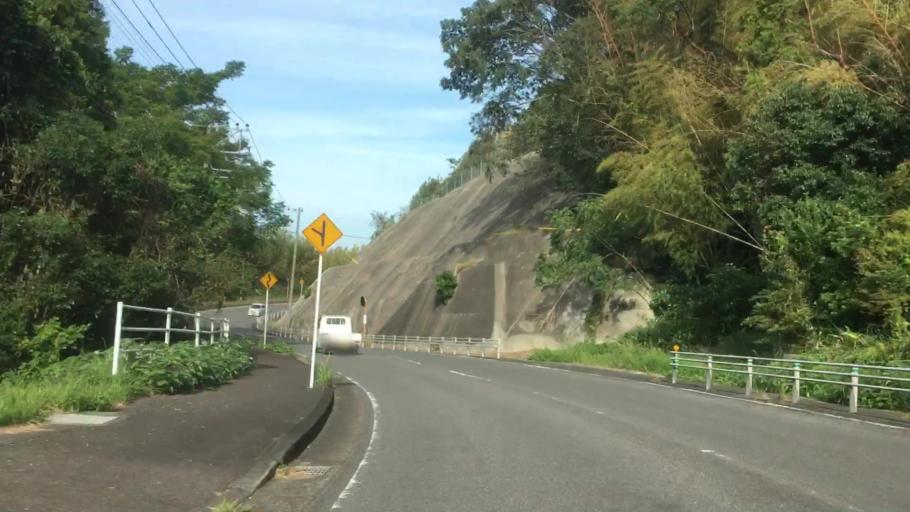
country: JP
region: Nagasaki
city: Sasebo
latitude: 33.0115
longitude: 129.6556
